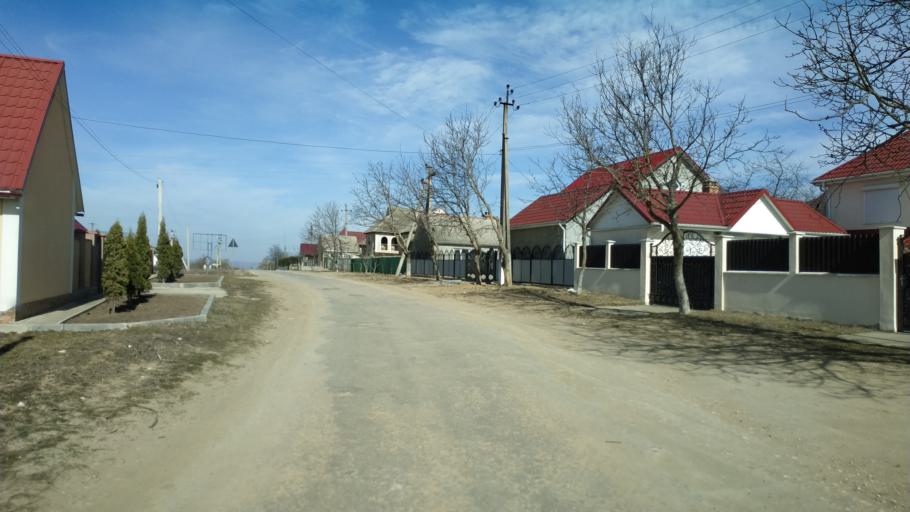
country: MD
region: Nisporeni
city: Nisporeni
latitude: 47.1025
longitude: 28.2962
